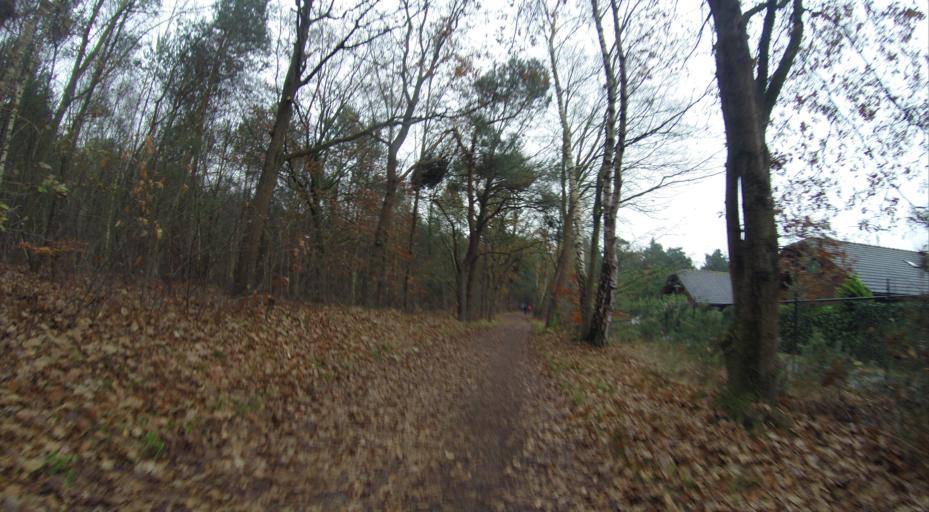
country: NL
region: Gelderland
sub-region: Gemeente Lochem
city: Lochem
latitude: 52.1394
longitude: 6.3843
